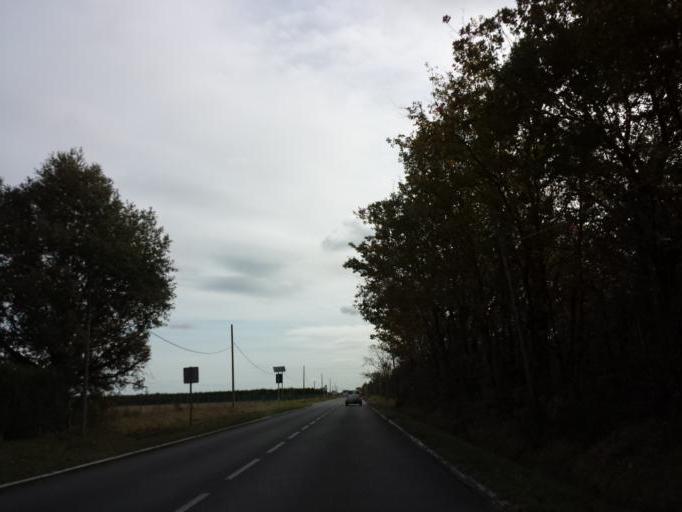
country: FR
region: Aquitaine
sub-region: Departement de la Gironde
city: Marcheprime
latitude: 44.7757
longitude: -0.9294
